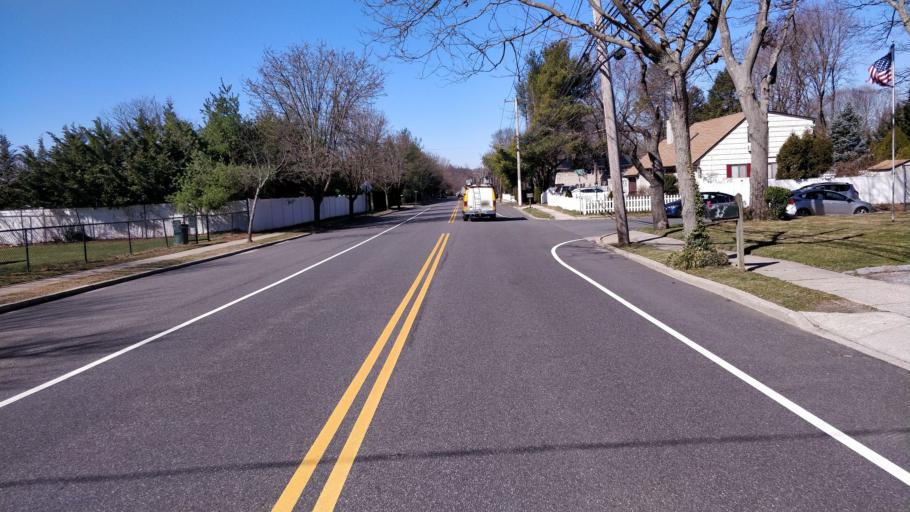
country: US
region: New York
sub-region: Suffolk County
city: Greenlawn
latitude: 40.8501
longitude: -73.3602
